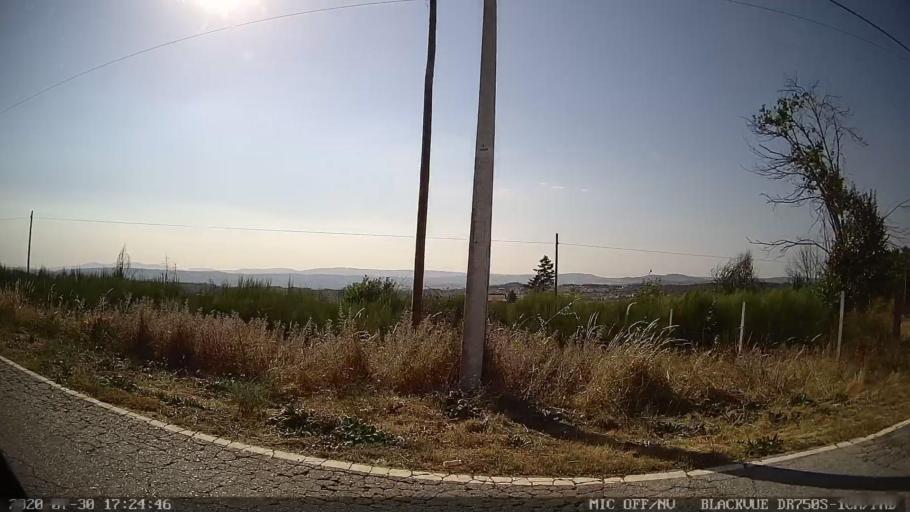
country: PT
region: Vila Real
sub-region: Murca
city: Murca
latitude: 41.3136
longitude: -7.4701
